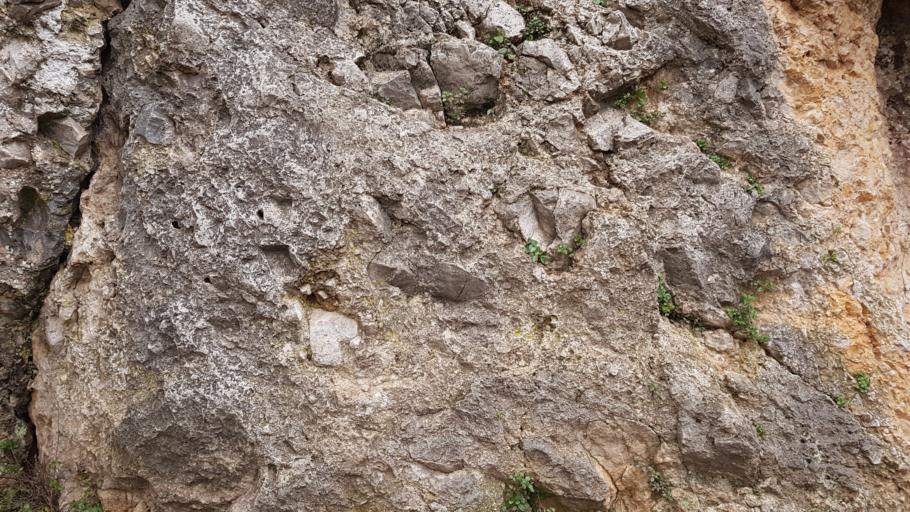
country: IT
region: Friuli Venezia Giulia
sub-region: Provincia di Gorizia
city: Doberdo del Lago
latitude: 45.8357
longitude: 13.5596
